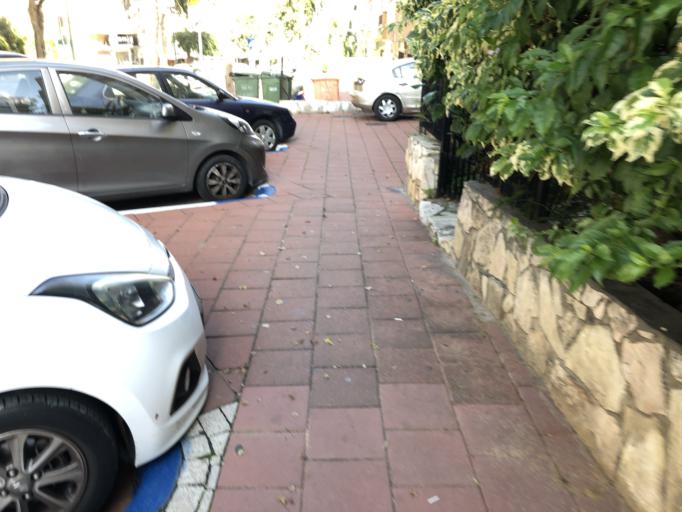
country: IL
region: Tel Aviv
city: Bene Beraq
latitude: 32.0725
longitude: 34.8249
